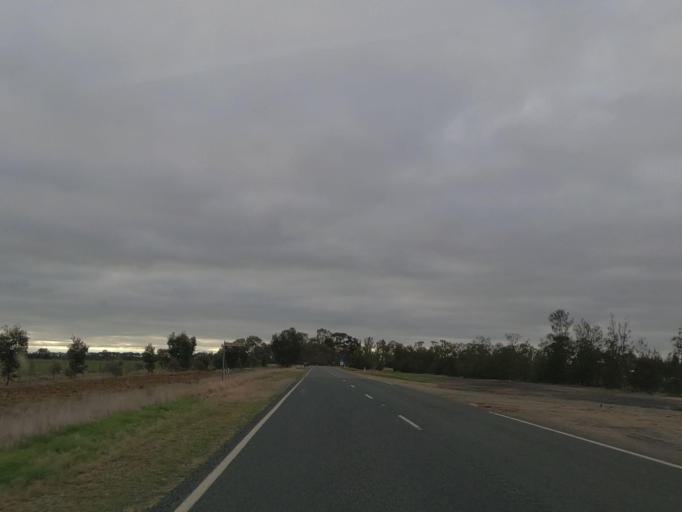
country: AU
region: Victoria
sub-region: Swan Hill
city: Swan Hill
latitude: -35.9515
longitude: 143.9413
